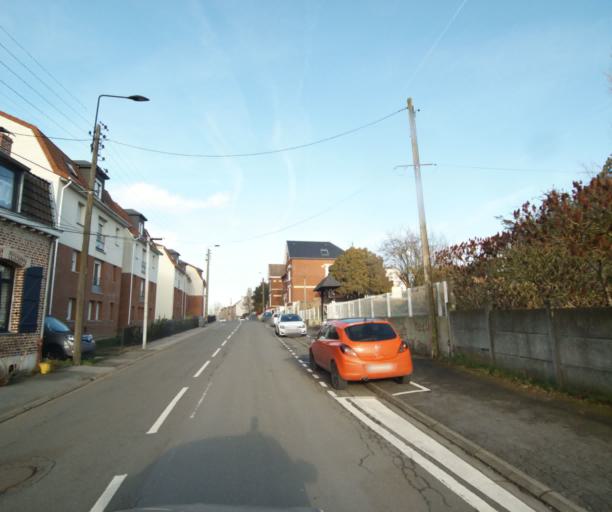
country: FR
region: Nord-Pas-de-Calais
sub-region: Departement du Nord
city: Saint-Saulve
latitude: 50.3641
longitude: 3.5426
